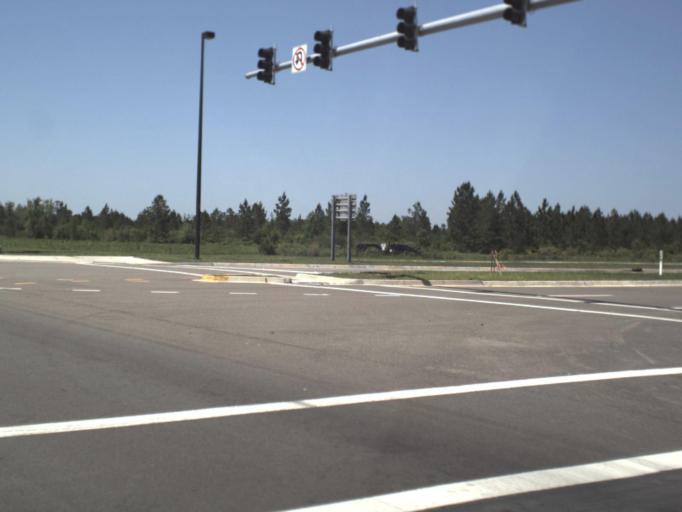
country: US
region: Florida
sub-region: Duval County
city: Baldwin
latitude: 30.2766
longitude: -81.8766
